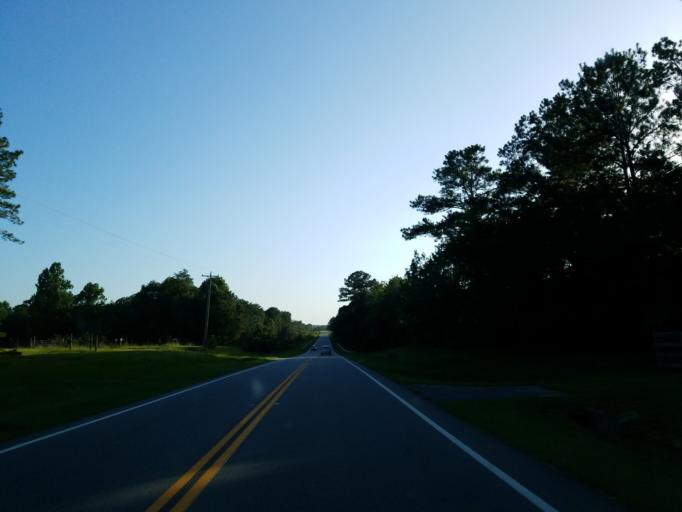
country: US
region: Georgia
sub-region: Irwin County
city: Ocilla
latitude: 31.6423
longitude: -83.3986
